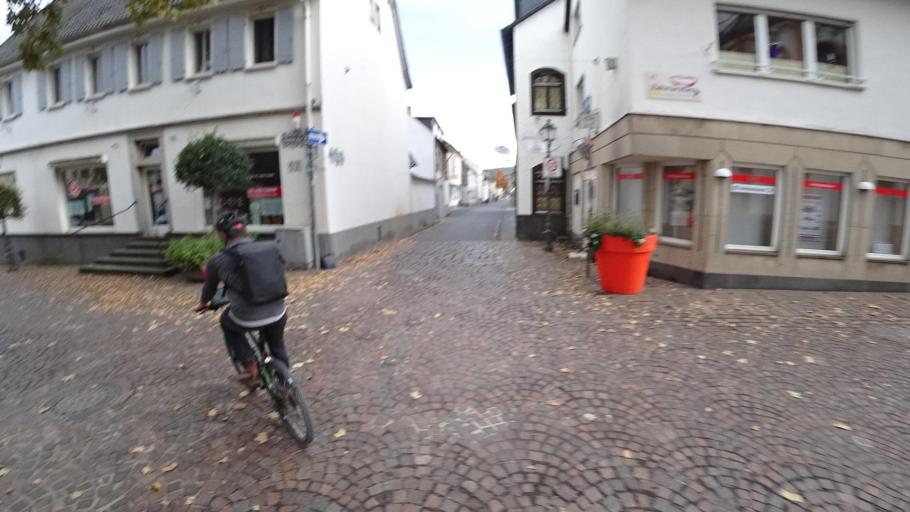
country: DE
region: Rheinland-Pfalz
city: Konigsfeld
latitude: 50.5435
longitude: 7.1761
